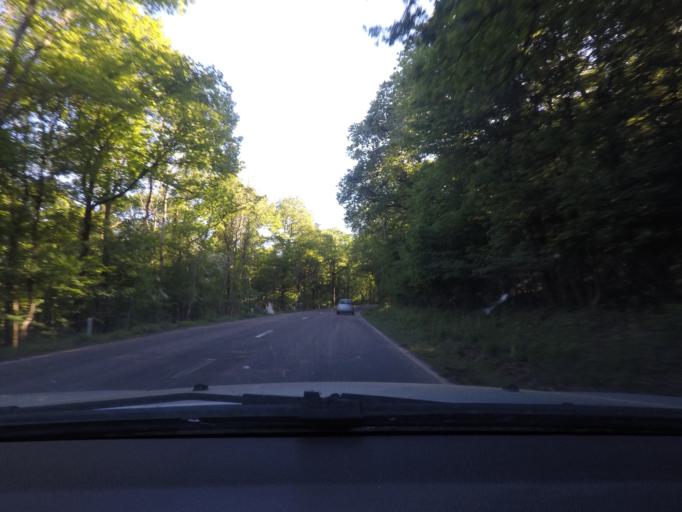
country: BE
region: Wallonia
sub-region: Province de Namur
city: Rochefort
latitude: 50.1929
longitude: 5.1292
